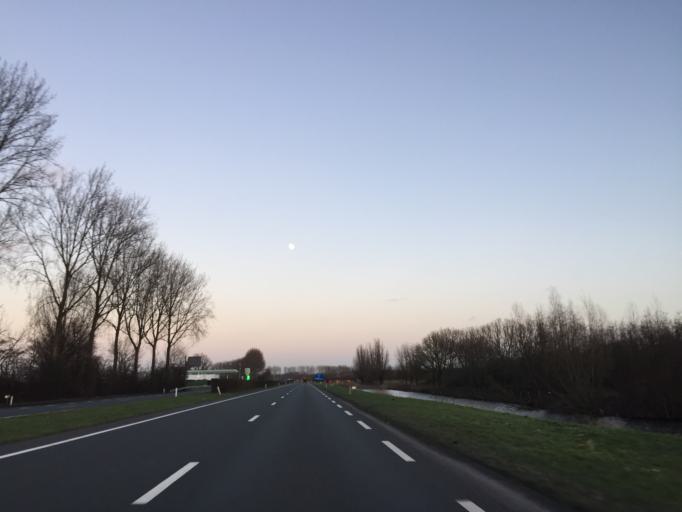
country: NL
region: South Holland
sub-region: Gemeente Lansingerland
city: Berkel en Rodenrijs
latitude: 51.9704
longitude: 4.4710
